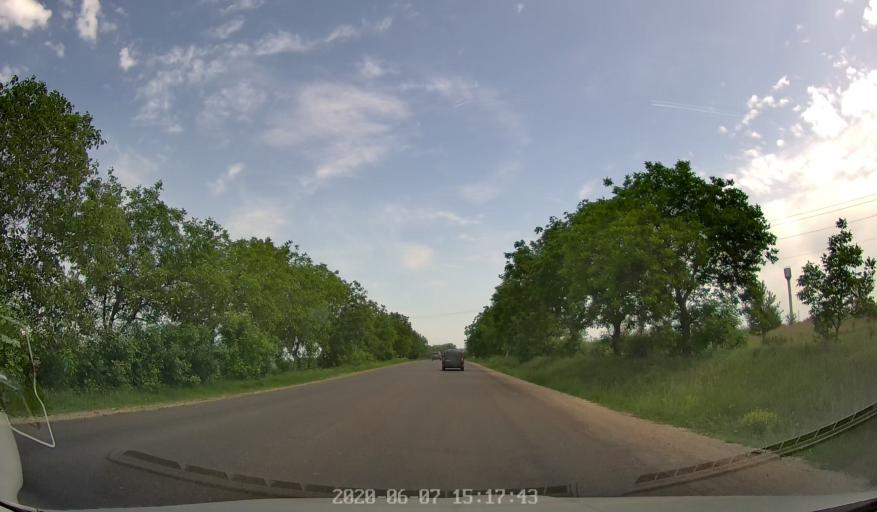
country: MD
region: Laloveni
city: Ialoveni
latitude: 46.9548
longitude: 28.7281
